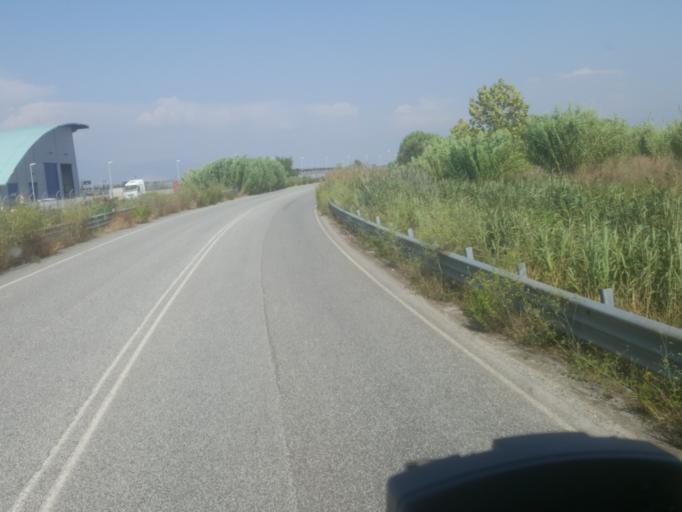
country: IT
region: Tuscany
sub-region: Provincia di Livorno
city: Guasticce
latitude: 43.6034
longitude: 10.4040
